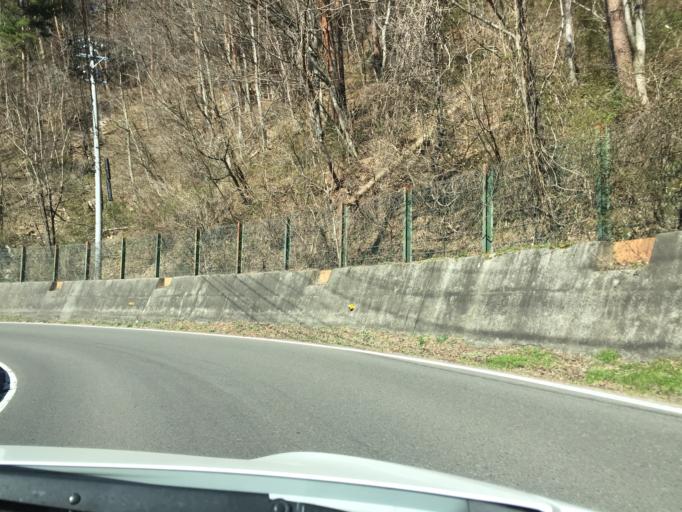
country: JP
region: Fukushima
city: Hobaramachi
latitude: 37.6452
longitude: 140.6278
